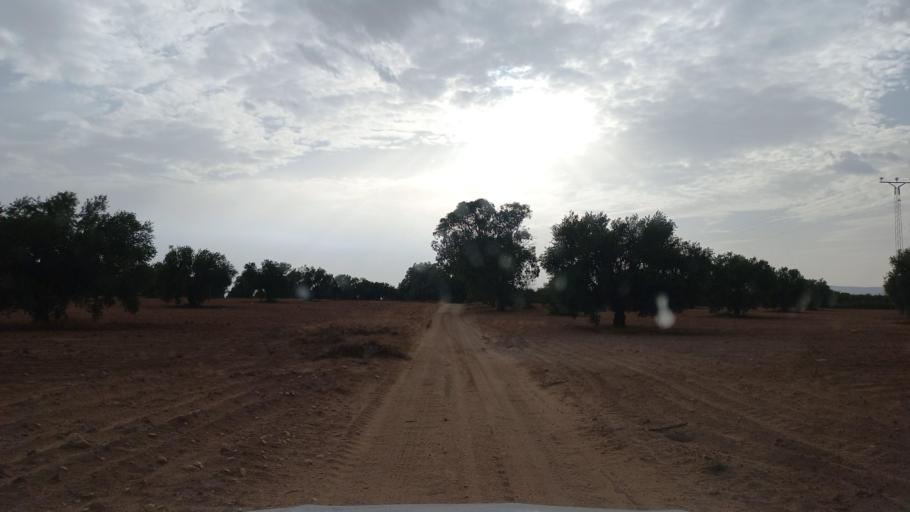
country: TN
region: Al Qasrayn
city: Sbiba
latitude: 35.2946
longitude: 9.0681
